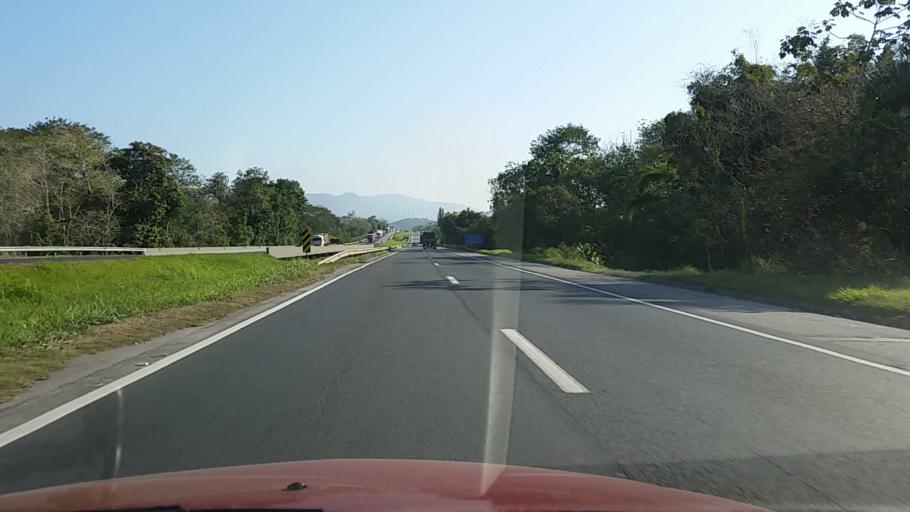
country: BR
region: Sao Paulo
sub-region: Miracatu
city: Miracatu
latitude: -24.2425
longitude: -47.3644
